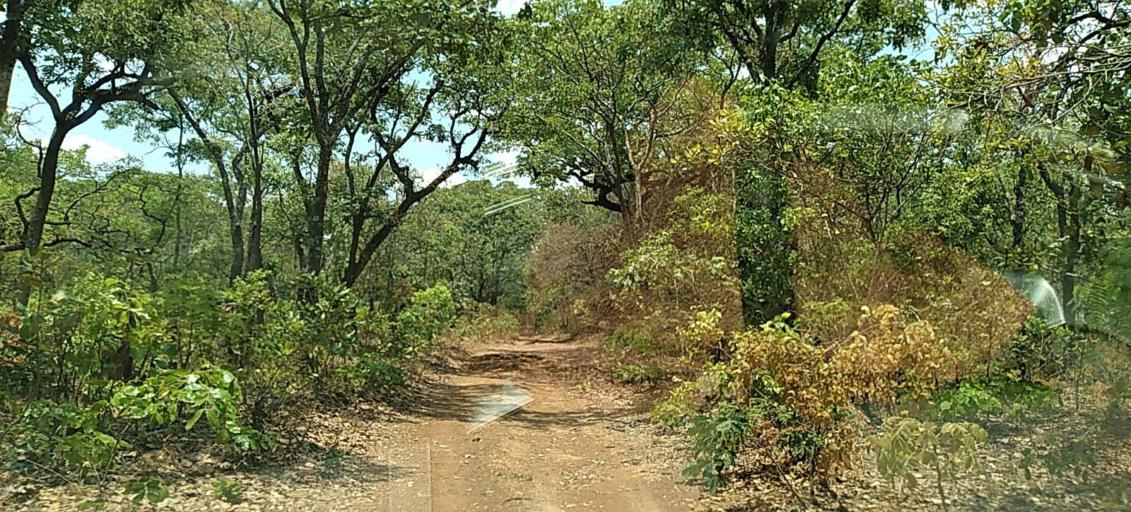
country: ZM
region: Copperbelt
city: Chililabombwe
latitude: -12.4477
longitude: 27.6961
